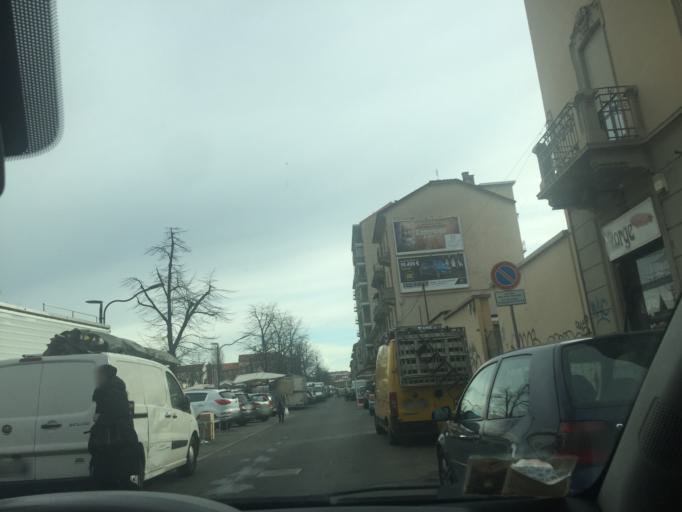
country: IT
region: Piedmont
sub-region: Provincia di Torino
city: Lesna
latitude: 45.0706
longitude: 7.6464
